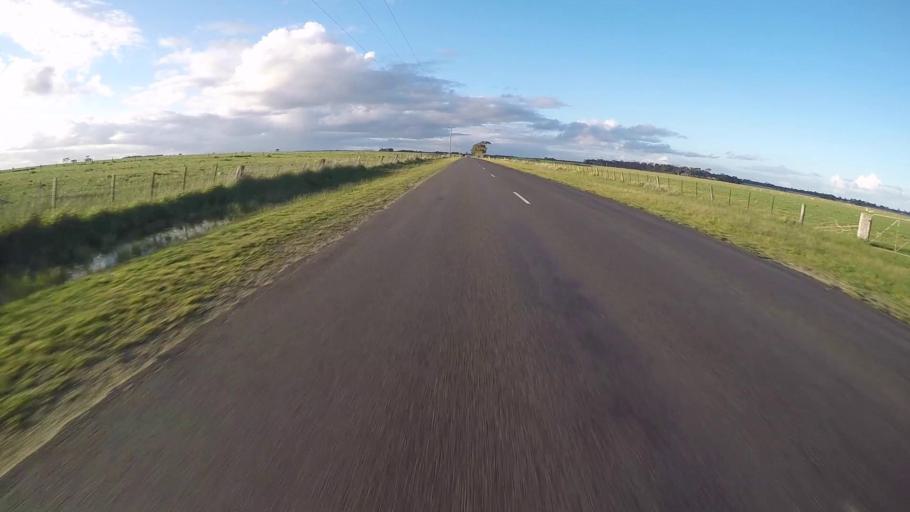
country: AU
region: Victoria
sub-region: Greater Geelong
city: Wandana Heights
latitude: -38.1321
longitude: 144.2009
